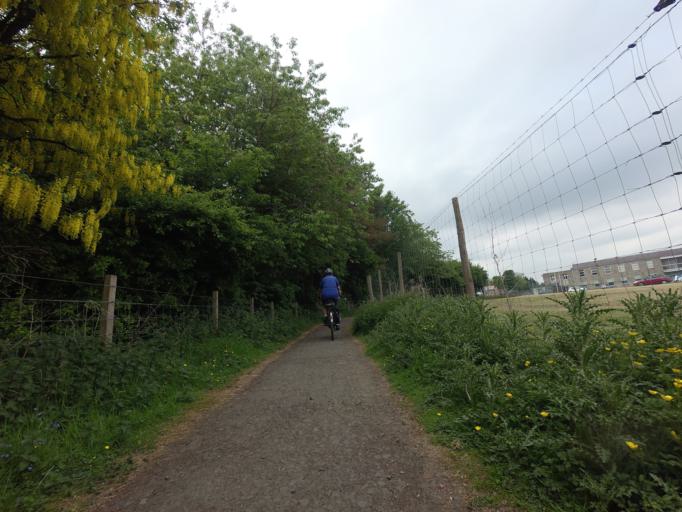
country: GB
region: Scotland
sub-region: Perth and Kinross
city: Kinross
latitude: 56.1971
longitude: -3.4225
